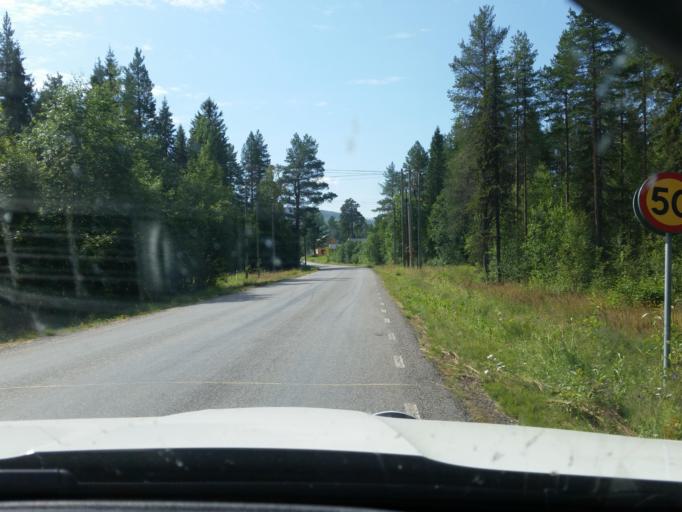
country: SE
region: Norrbotten
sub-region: Alvsbyns Kommun
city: AElvsbyn
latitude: 65.6740
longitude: 20.8745
